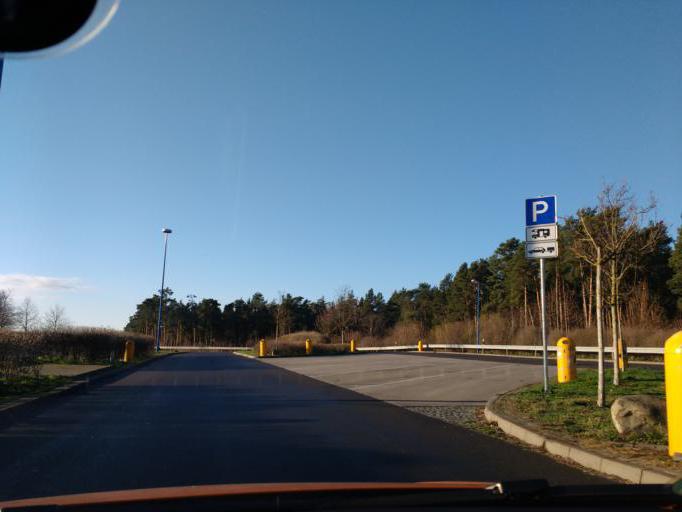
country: DE
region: Brandenburg
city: Ziesar
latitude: 52.2512
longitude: 12.3057
